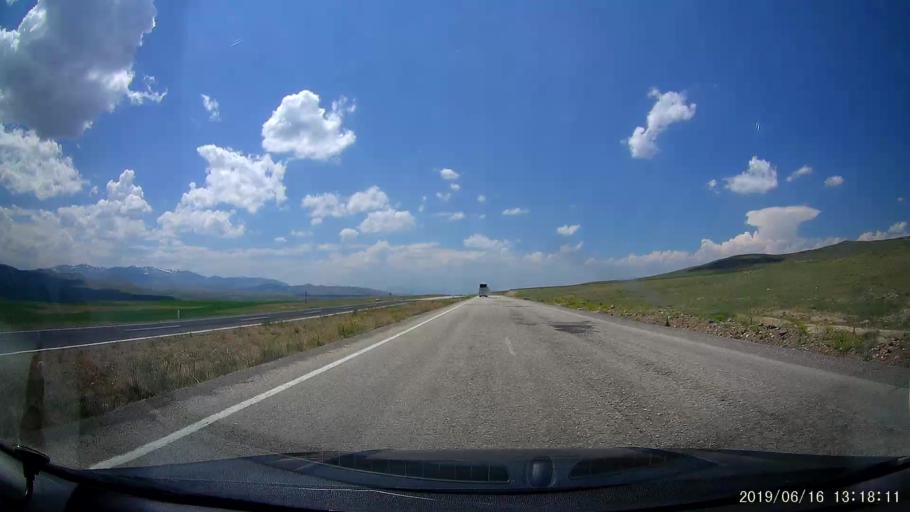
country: TR
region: Agri
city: Taslicay
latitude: 39.6296
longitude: 43.4363
